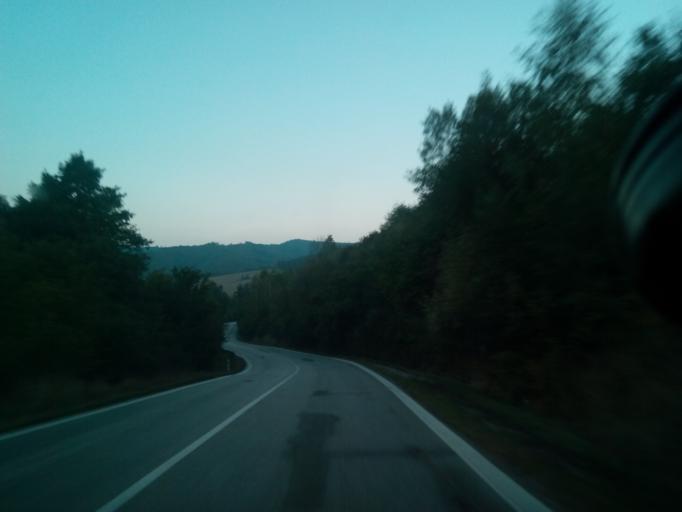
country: SK
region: Kosicky
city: Dobsina
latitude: 48.7317
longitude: 20.4152
